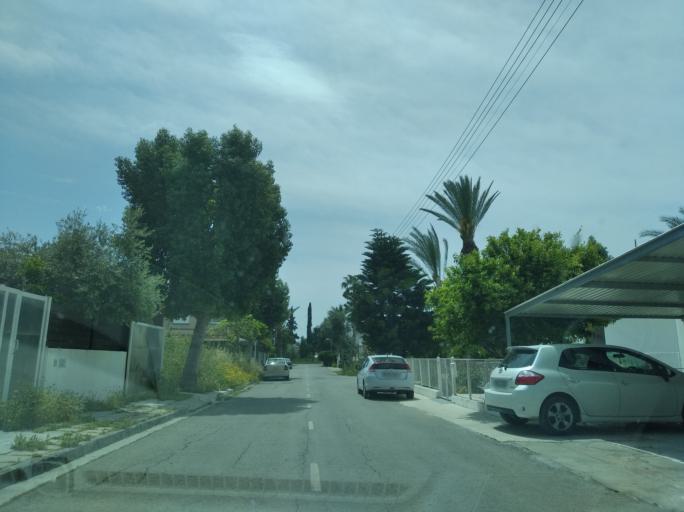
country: CY
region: Lefkosia
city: Nicosia
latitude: 35.1901
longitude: 33.3776
